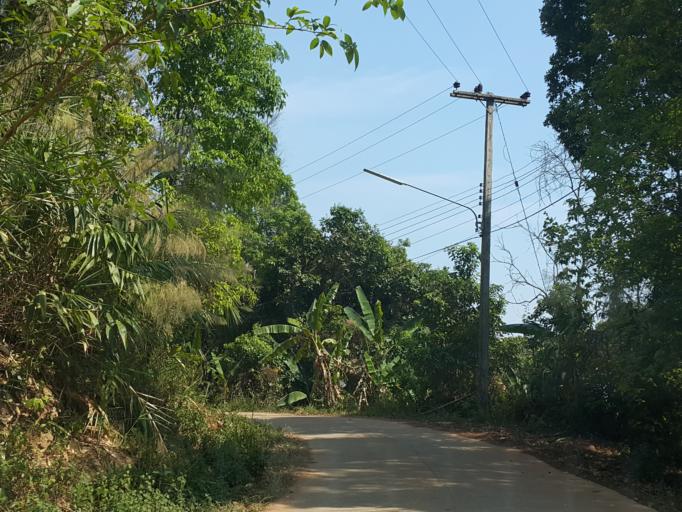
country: TH
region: Chiang Mai
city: Samoeng
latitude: 18.8866
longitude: 98.7872
